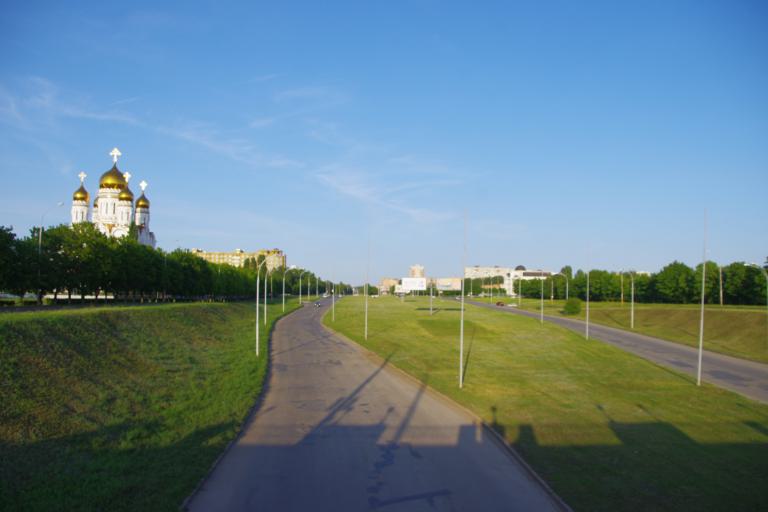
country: RU
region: Samara
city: Tol'yatti
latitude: 53.5204
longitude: 49.2742
